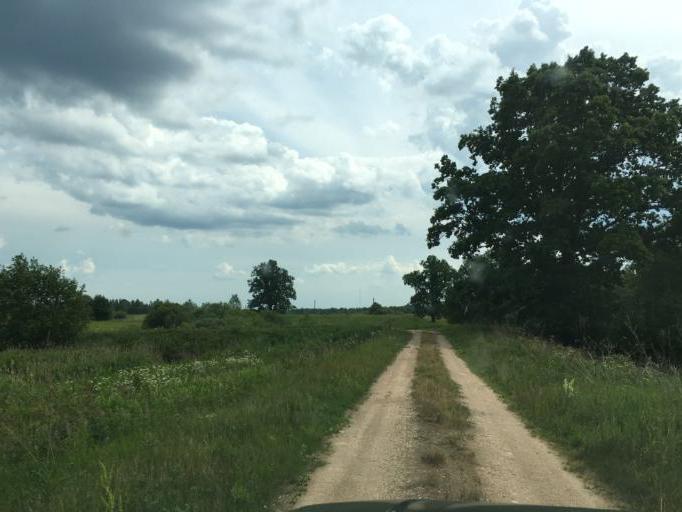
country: LV
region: Rugaju
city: Rugaji
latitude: 56.9766
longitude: 27.0508
